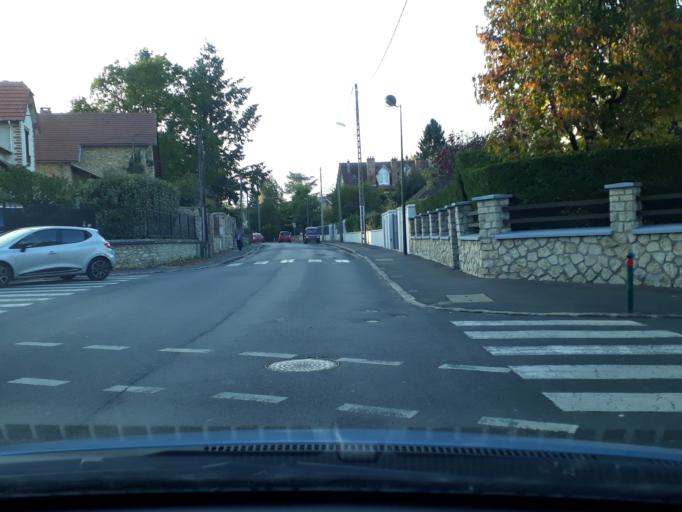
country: FR
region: Ile-de-France
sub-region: Departement de Seine-et-Marne
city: Bois-le-Roi
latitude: 48.4720
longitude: 2.7004
